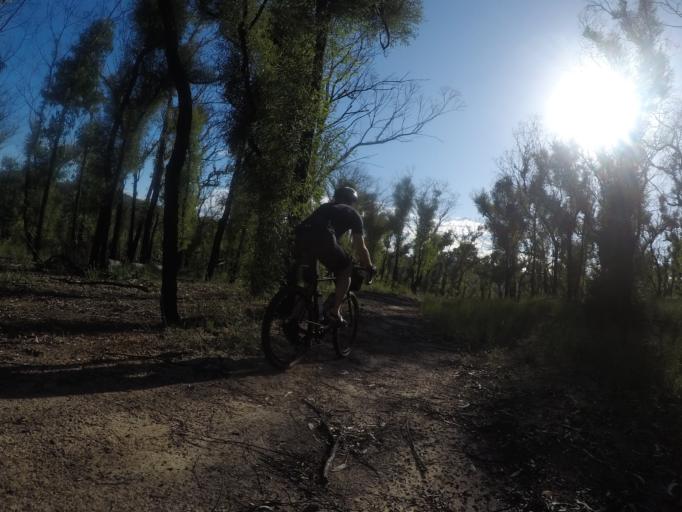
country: AU
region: New South Wales
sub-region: Hornsby Shire
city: Glenorie
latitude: -33.3497
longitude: 151.0350
